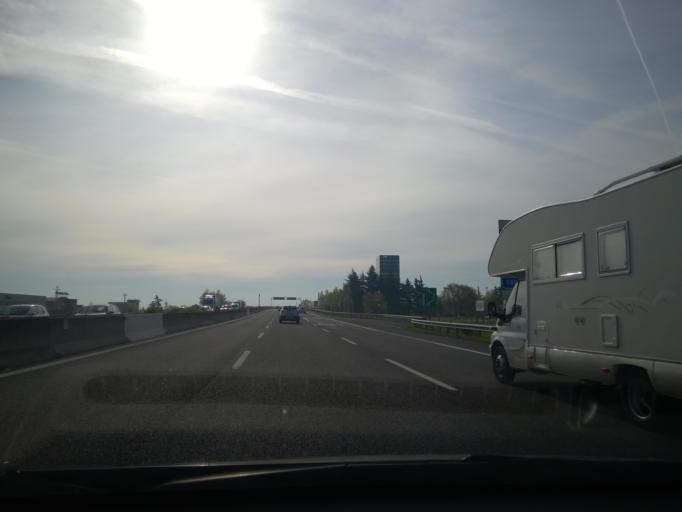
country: IT
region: Emilia-Romagna
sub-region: Provincia di Bologna
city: Imola
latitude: 44.3831
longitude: 11.7352
